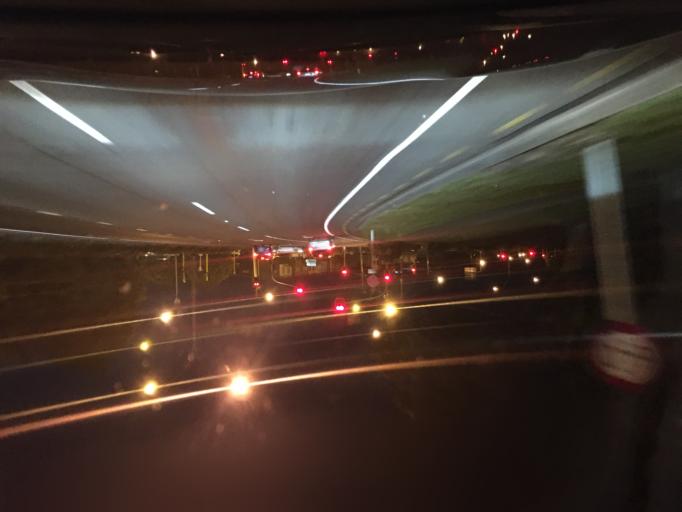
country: NZ
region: Waikato
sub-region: Hamilton City
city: Hamilton
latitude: -37.8068
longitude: 175.2865
